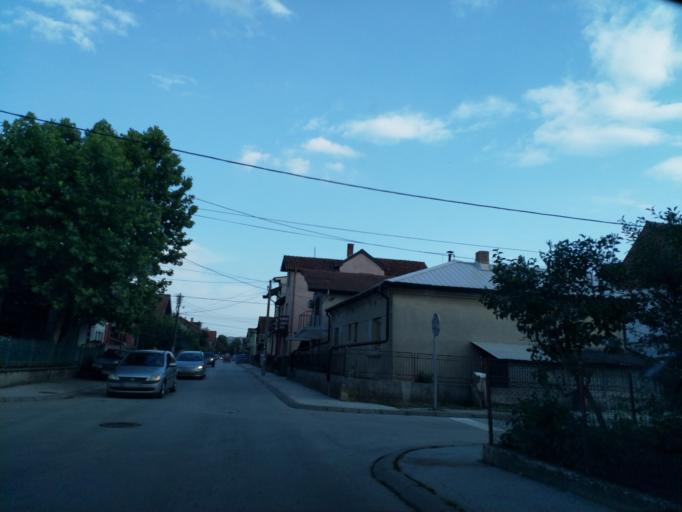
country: RS
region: Central Serbia
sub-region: Pomoravski Okrug
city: Jagodina
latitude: 43.9827
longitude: 21.2432
